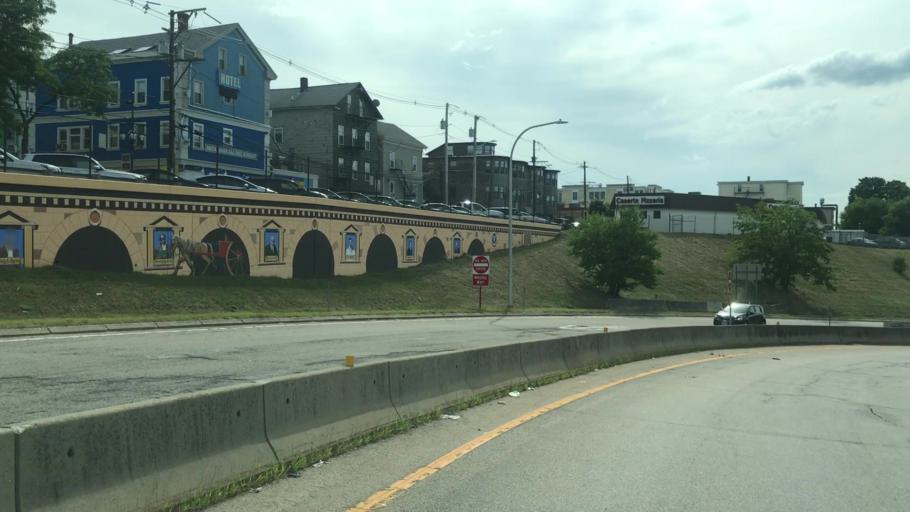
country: US
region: Rhode Island
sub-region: Providence County
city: Providence
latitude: 41.8244
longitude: -71.4264
